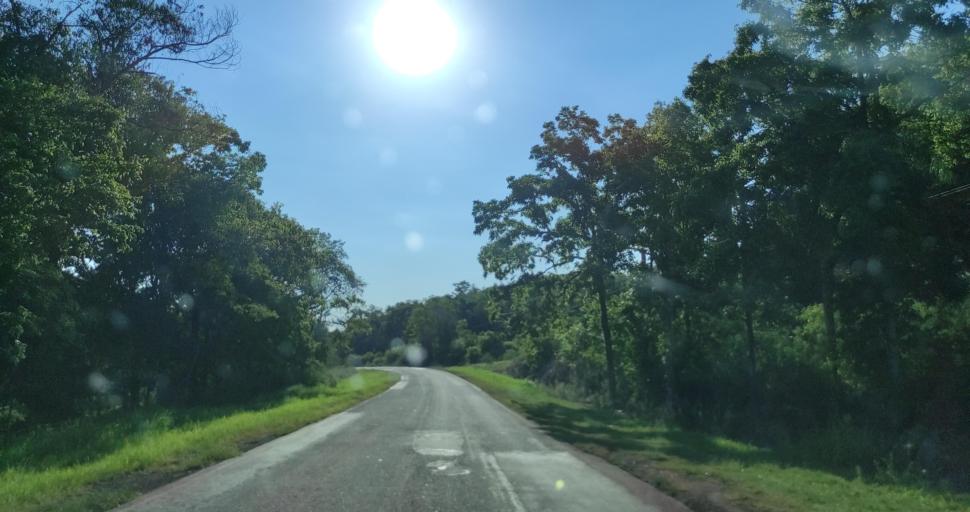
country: AR
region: Misiones
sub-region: Departamento de Eldorado
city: Eldorado
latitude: -26.4004
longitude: -54.4224
